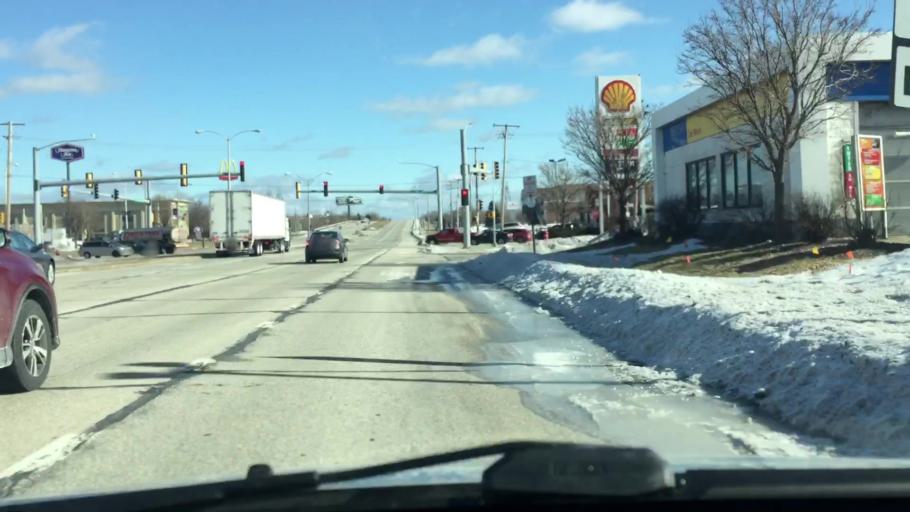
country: US
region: Wisconsin
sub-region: Milwaukee County
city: Saint Francis
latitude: 42.9302
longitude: -87.9311
